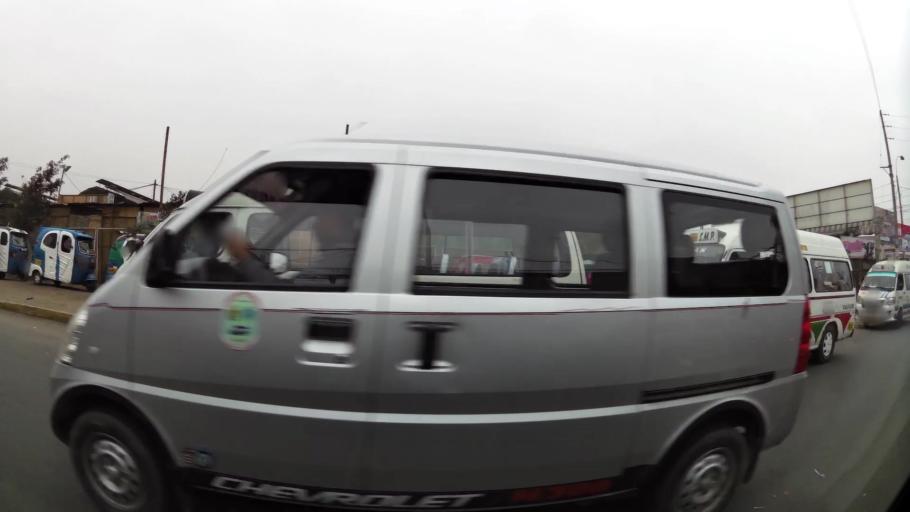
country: PE
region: Lima
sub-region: Lima
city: Independencia
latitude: -11.9376
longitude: -77.0709
